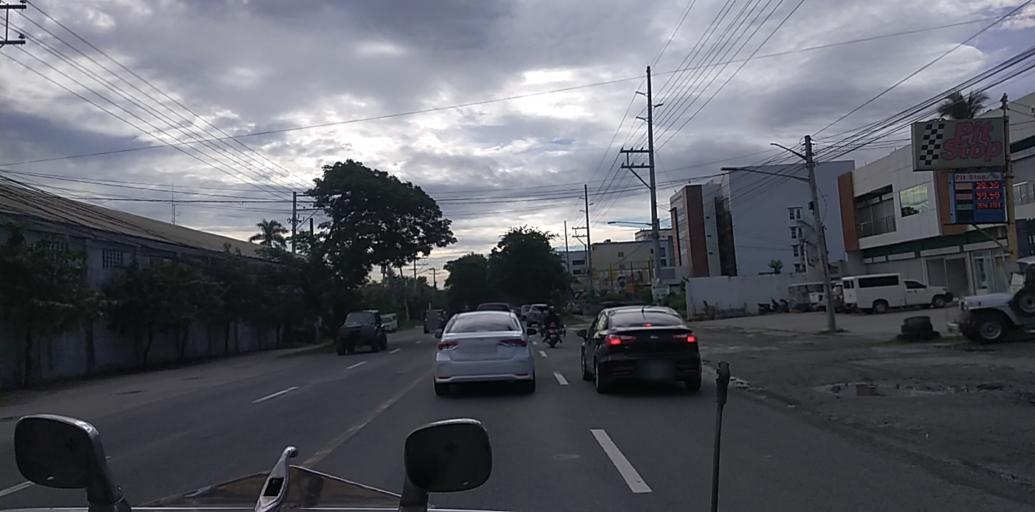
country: PH
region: Central Luzon
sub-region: Province of Pampanga
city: Telabastagan
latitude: 15.0978
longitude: 120.6230
